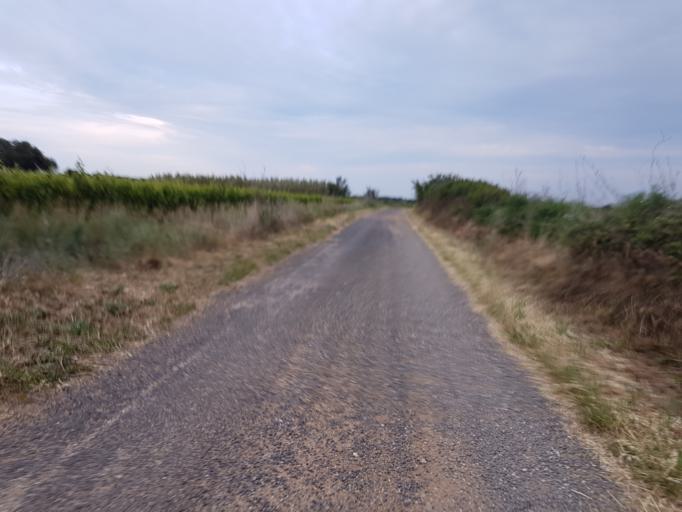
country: FR
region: Languedoc-Roussillon
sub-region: Departement de l'Herault
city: Portiragnes
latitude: 43.3173
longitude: 3.3297
